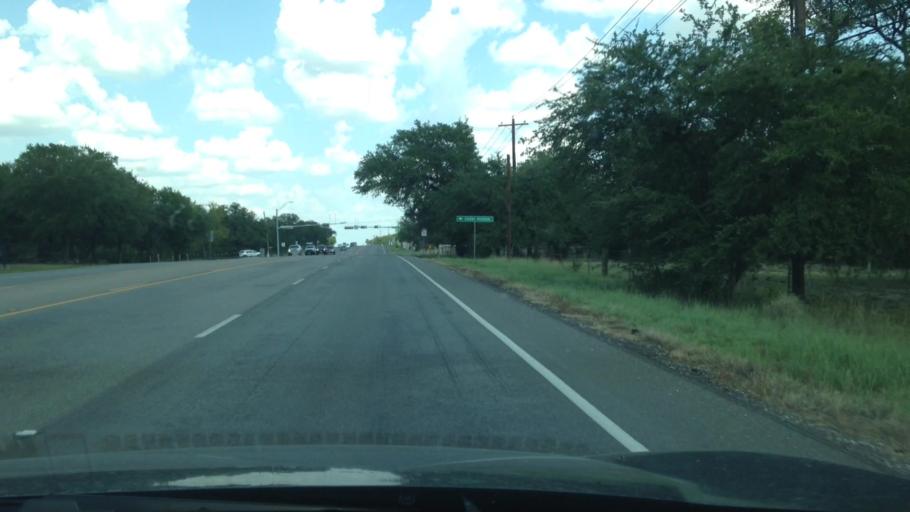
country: US
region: Texas
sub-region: Williamson County
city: Georgetown
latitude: 30.6328
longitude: -97.7670
